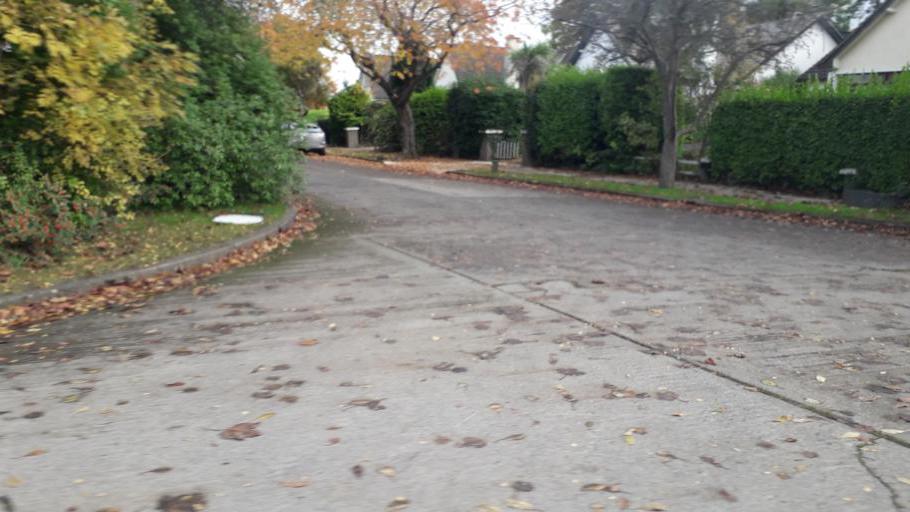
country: IE
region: Leinster
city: Mount Merrion
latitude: 53.2969
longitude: -6.2278
